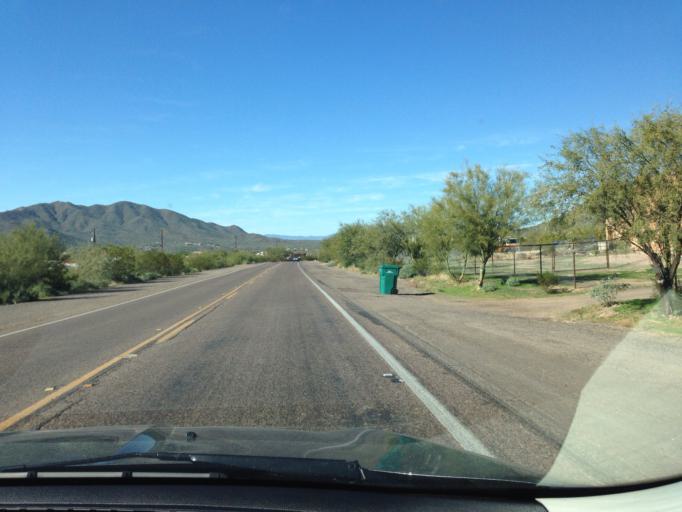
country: US
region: Arizona
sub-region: Maricopa County
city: Anthem
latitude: 33.8663
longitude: -112.0598
